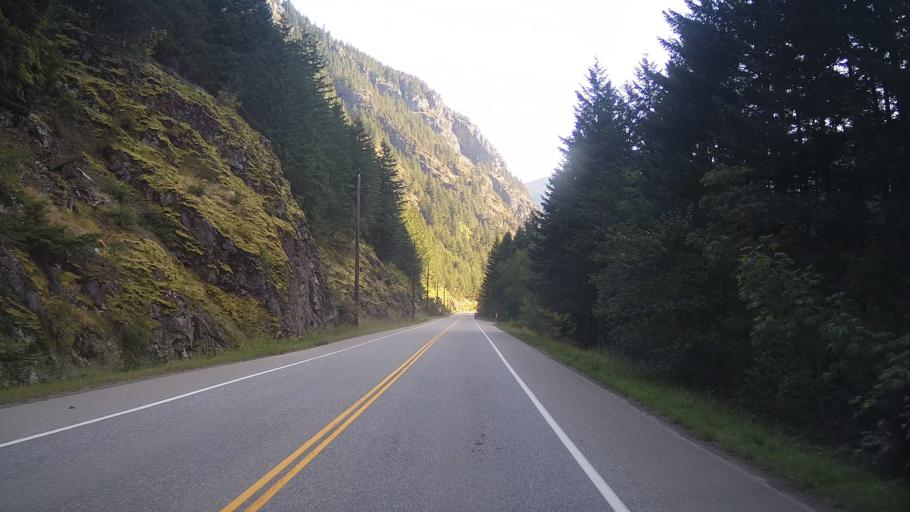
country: CA
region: British Columbia
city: Hope
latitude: 49.6106
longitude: -121.4143
